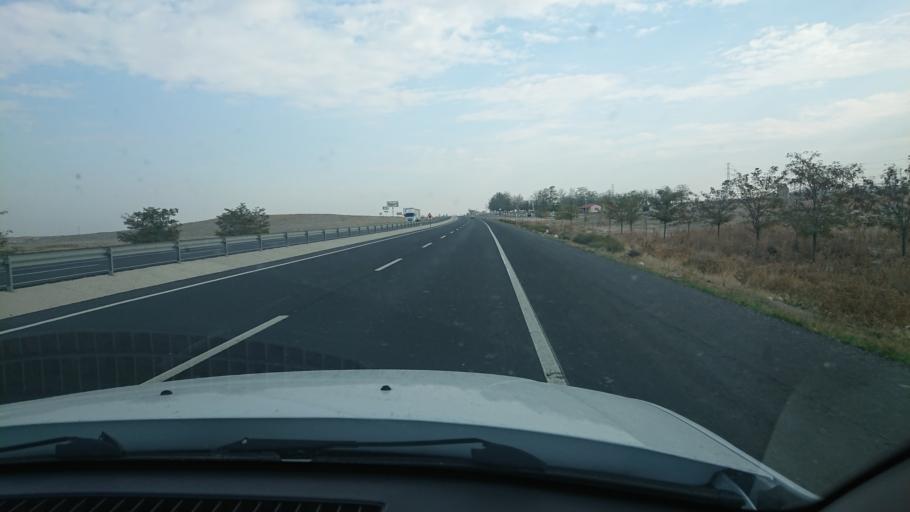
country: TR
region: Aksaray
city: Yesilova
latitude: 38.2949
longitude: 33.7765
